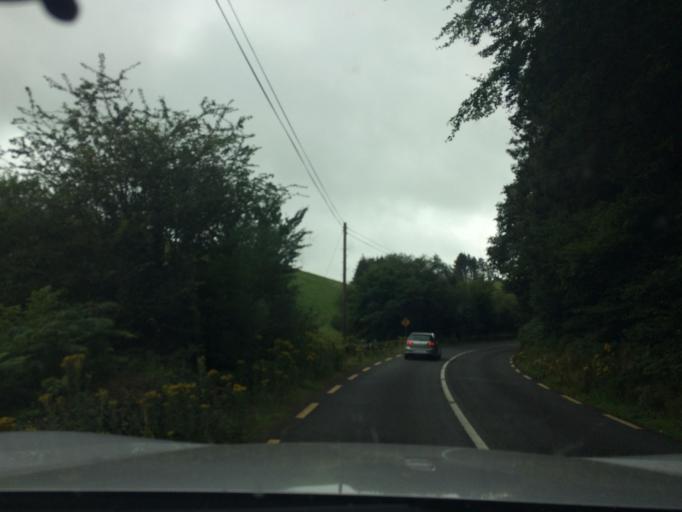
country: IE
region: Munster
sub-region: South Tipperary
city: Cluain Meala
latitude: 52.2520
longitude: -7.7127
